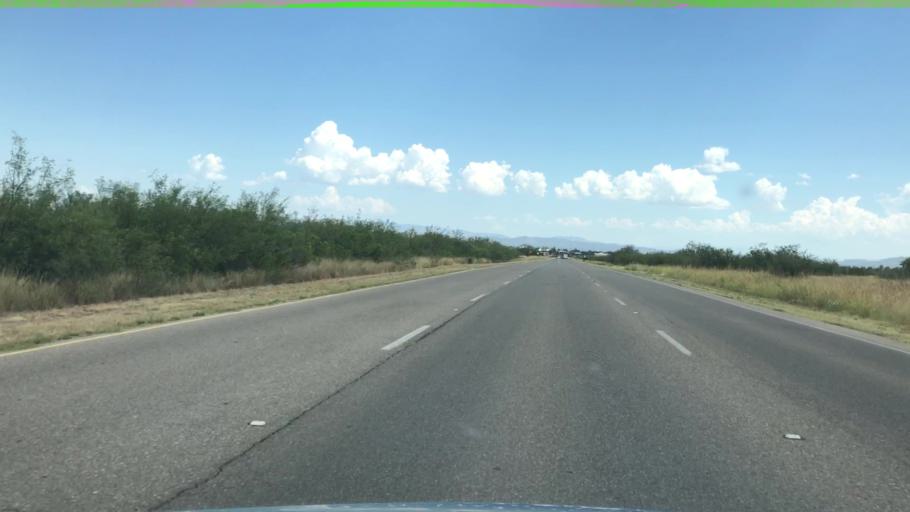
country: US
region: Arizona
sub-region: Cochise County
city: Sierra Vista
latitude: 31.5465
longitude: -110.3224
